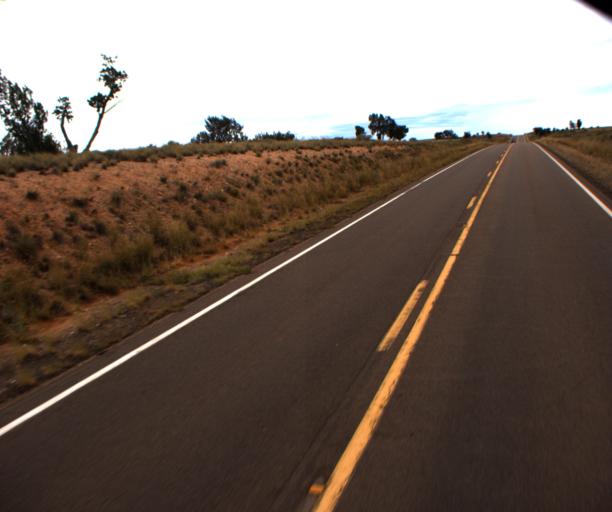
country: US
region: Arizona
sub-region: Navajo County
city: Snowflake
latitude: 34.6105
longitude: -110.0902
